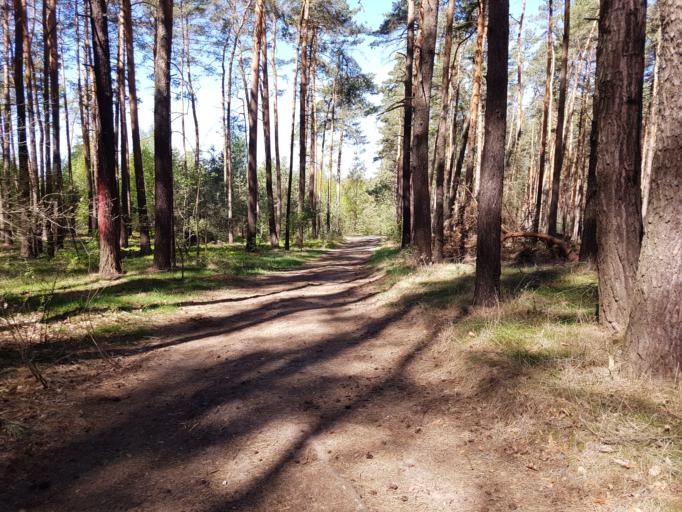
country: DE
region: Brandenburg
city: Groden
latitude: 51.3916
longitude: 13.5734
